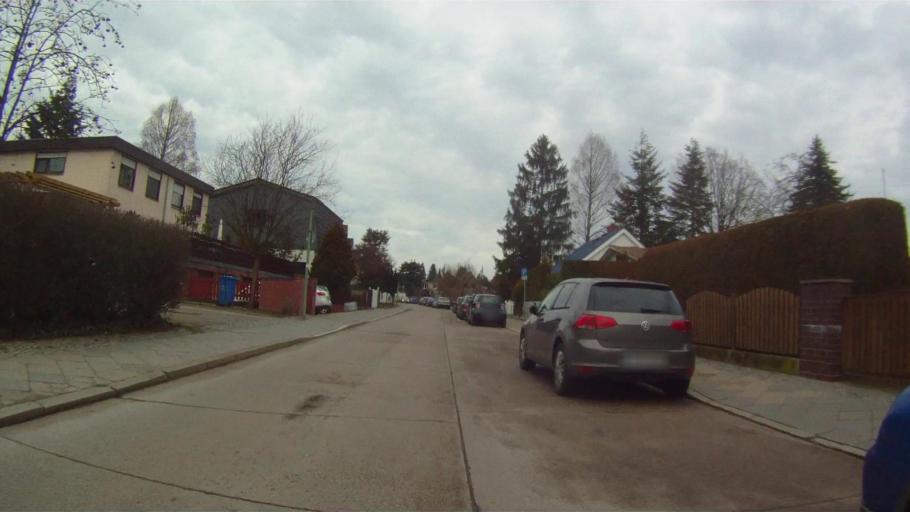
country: DE
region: Berlin
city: Lichtenrade
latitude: 52.3934
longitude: 13.3862
